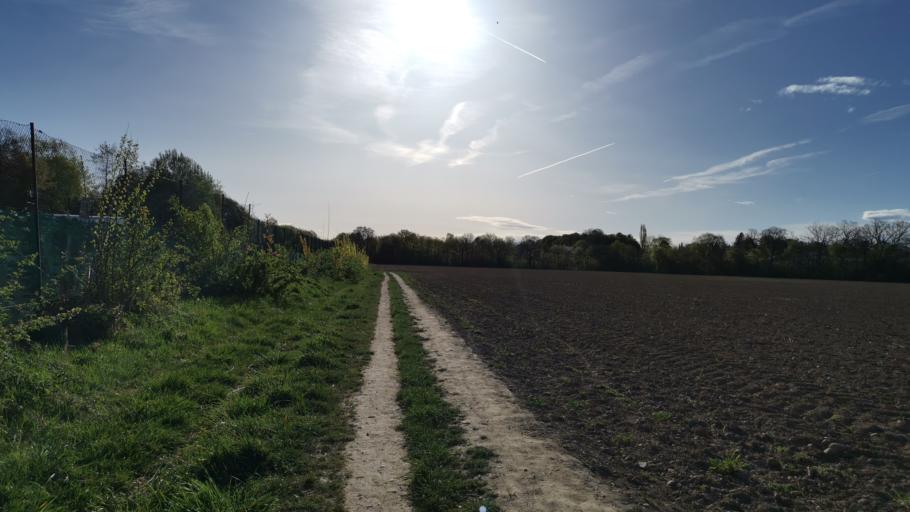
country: DE
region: Bavaria
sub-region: Upper Bavaria
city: Pullach im Isartal
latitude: 48.0881
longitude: 11.5243
